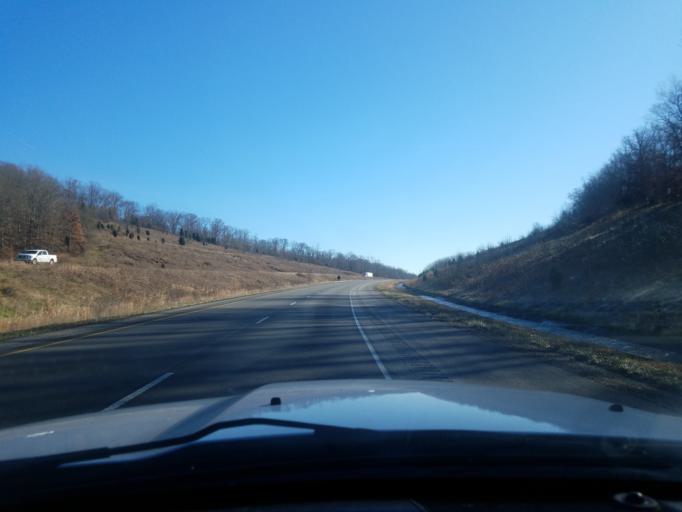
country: US
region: Indiana
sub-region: Crawford County
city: English
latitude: 38.2382
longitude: -86.5169
